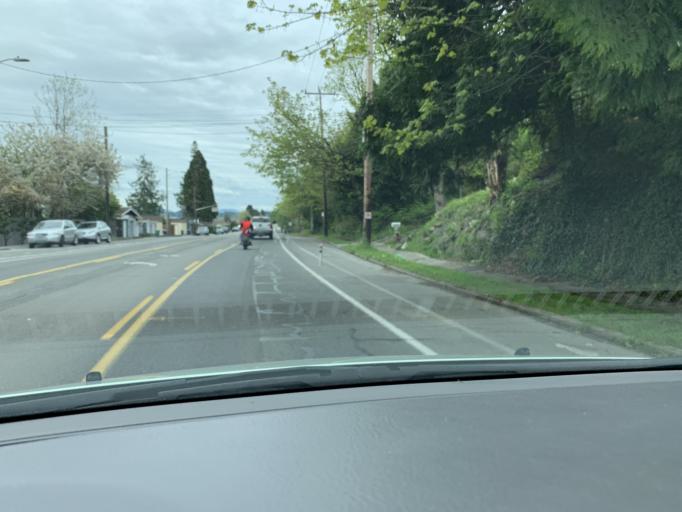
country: US
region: Washington
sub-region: King County
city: Bryn Mawr-Skyway
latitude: 47.5104
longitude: -122.2388
